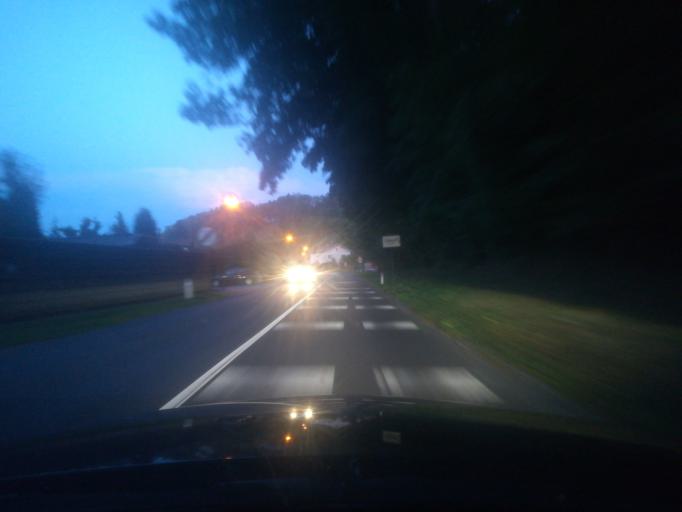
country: AT
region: Upper Austria
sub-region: Wels-Land
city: Marchtrenk
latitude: 48.1626
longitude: 14.0894
